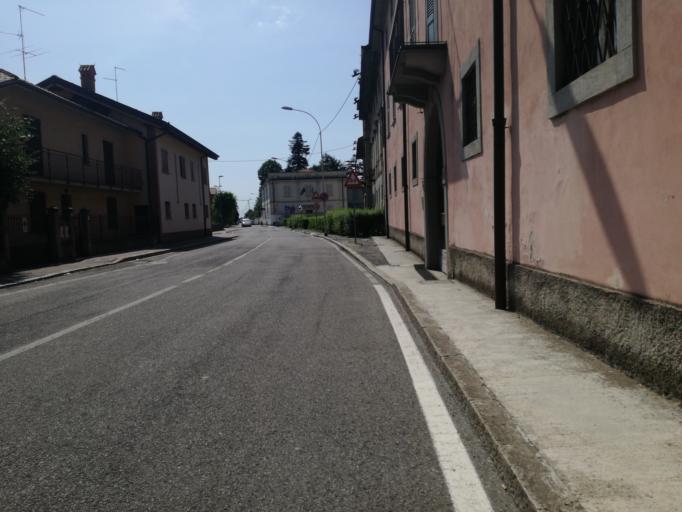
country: IT
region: Lombardy
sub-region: Provincia di Bergamo
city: Calusco d'Adda
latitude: 45.6856
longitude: 9.4788
